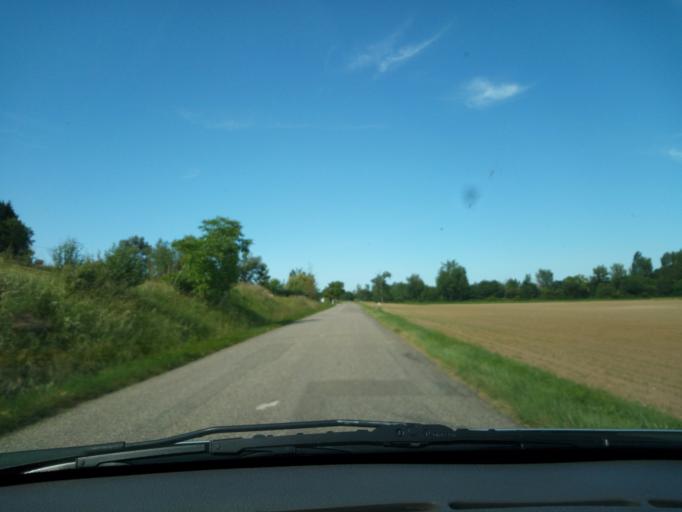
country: FR
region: Midi-Pyrenees
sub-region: Departement du Tarn-et-Garonne
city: Molieres
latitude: 44.2012
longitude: 1.3016
